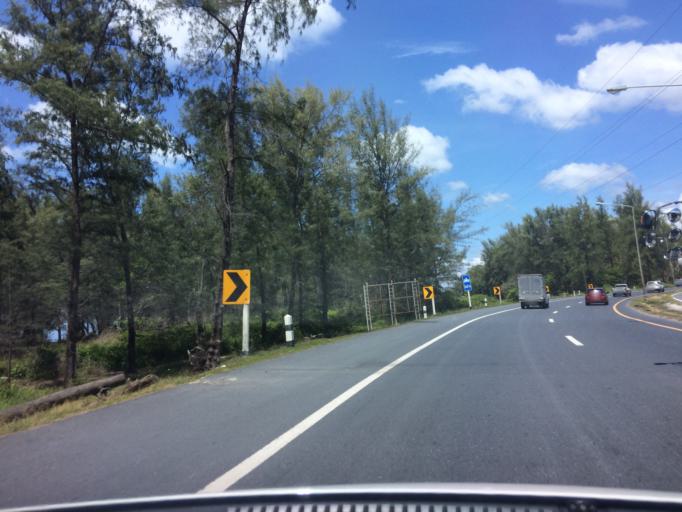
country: TH
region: Phuket
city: Thalang
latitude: 8.1897
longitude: 98.2879
